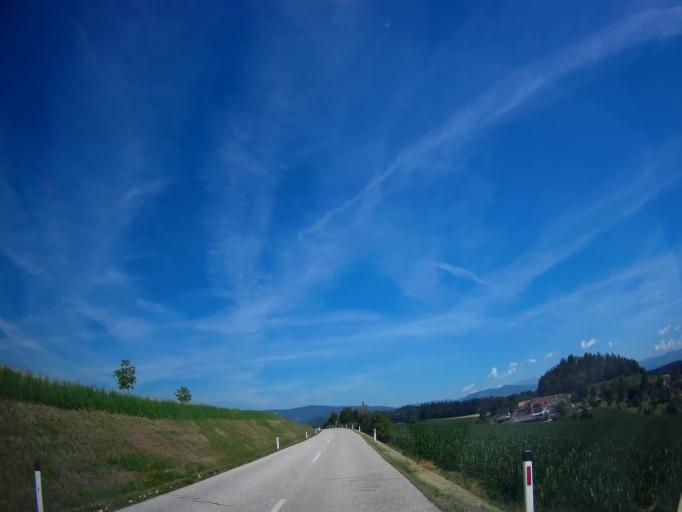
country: AT
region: Carinthia
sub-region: Politischer Bezirk Sankt Veit an der Glan
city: St. Georgen am Laengsee
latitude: 46.7926
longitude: 14.4181
